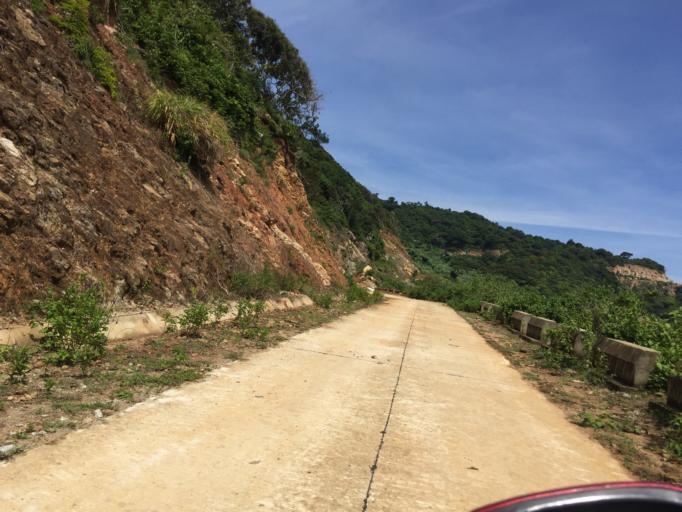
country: VN
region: Quang Nam
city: Hoi An
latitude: 15.9677
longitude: 108.5083
